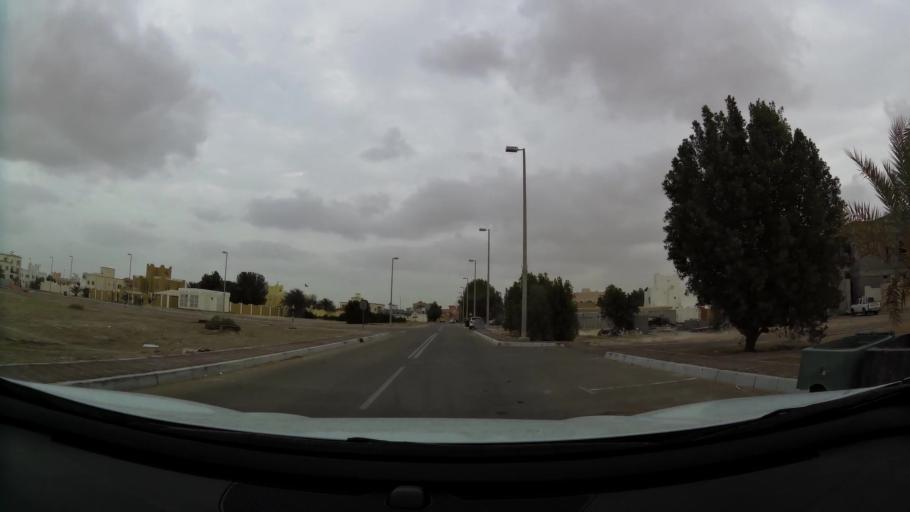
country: AE
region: Abu Dhabi
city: Abu Dhabi
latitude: 24.3839
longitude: 54.6552
